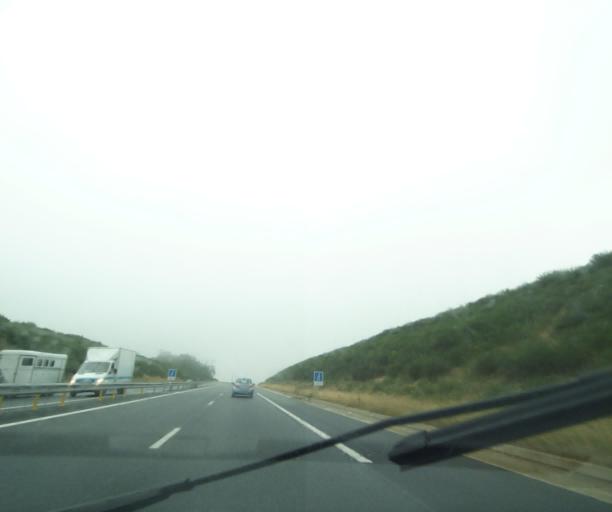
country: FR
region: Midi-Pyrenees
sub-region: Departement de l'Aveyron
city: Baraqueville
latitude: 44.2187
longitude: 2.4070
